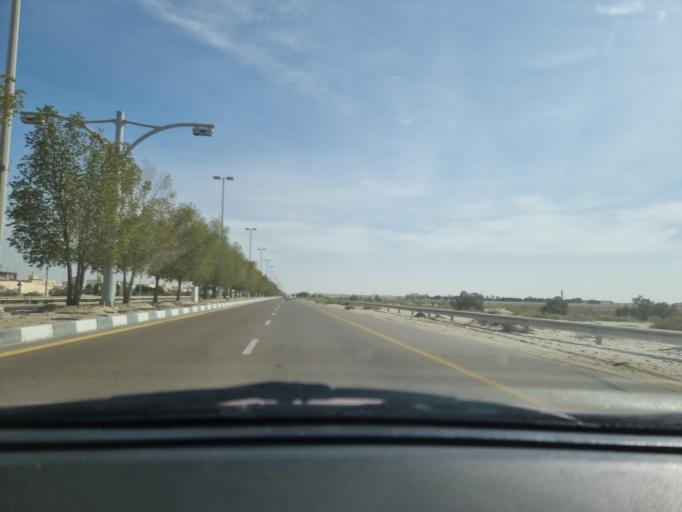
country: AE
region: Abu Dhabi
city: Abu Dhabi
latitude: 24.3846
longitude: 54.6823
